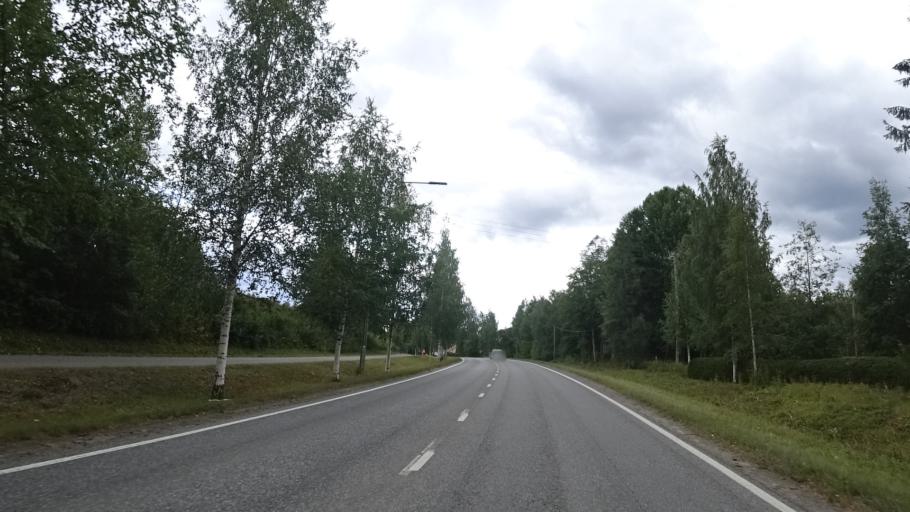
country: FI
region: North Karelia
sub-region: Joensuu
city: Ilomantsi
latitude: 62.6602
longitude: 30.9339
